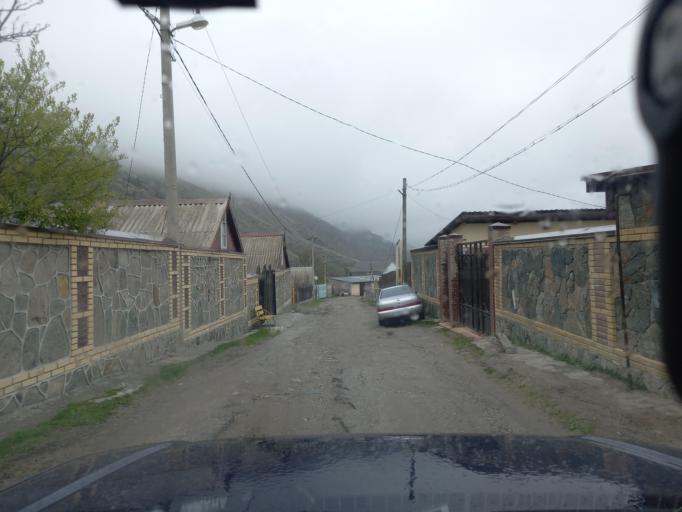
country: RU
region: Kabardino-Balkariya
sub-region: El'brusskiy Rayon
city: El'brus
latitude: 43.2606
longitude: 42.6482
